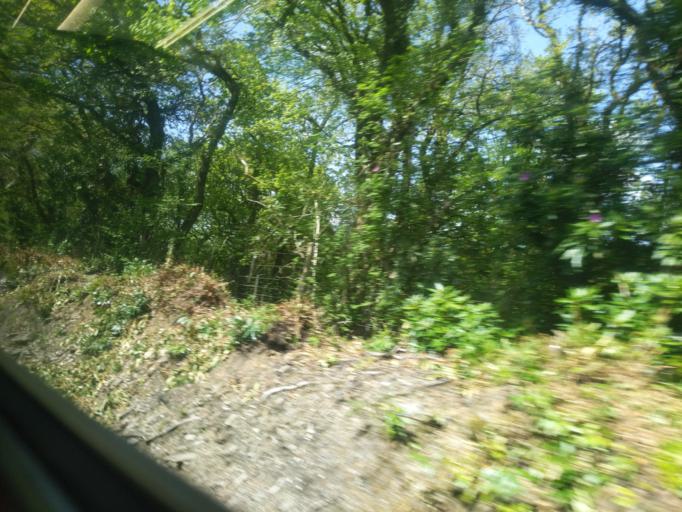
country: GB
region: England
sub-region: Cornwall
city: Liskeard
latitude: 50.4529
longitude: -4.5633
